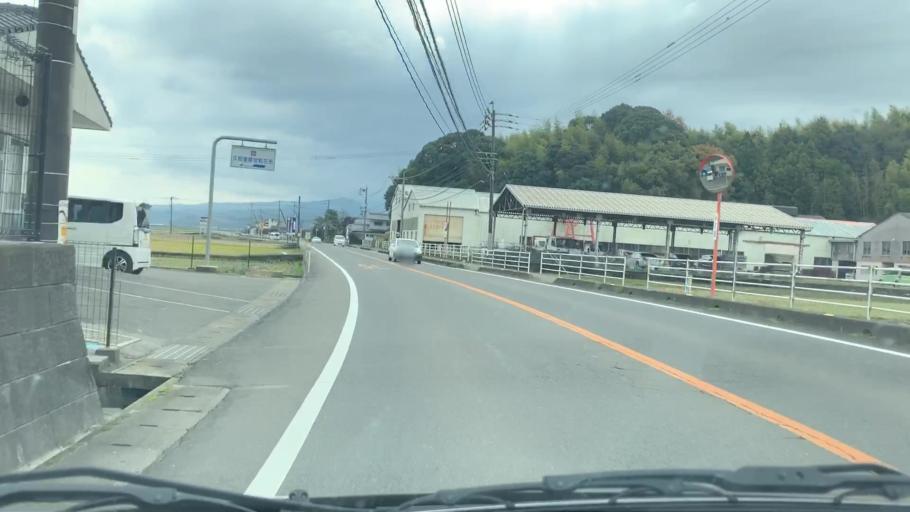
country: JP
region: Saga Prefecture
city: Kashima
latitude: 33.1465
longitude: 130.0629
